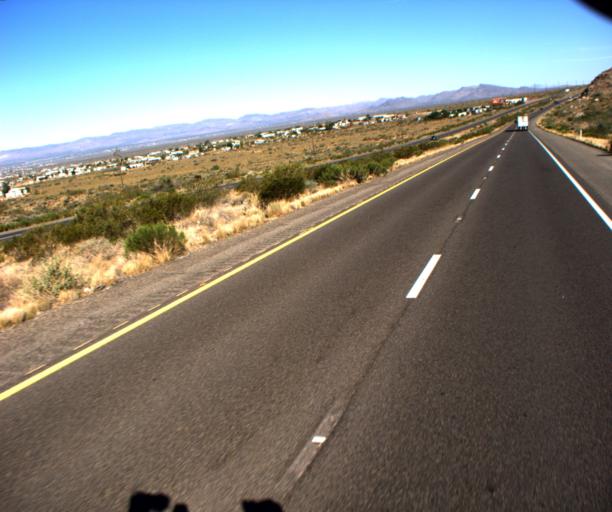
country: US
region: Arizona
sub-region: Mohave County
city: Golden Valley
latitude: 35.2377
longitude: -114.1424
